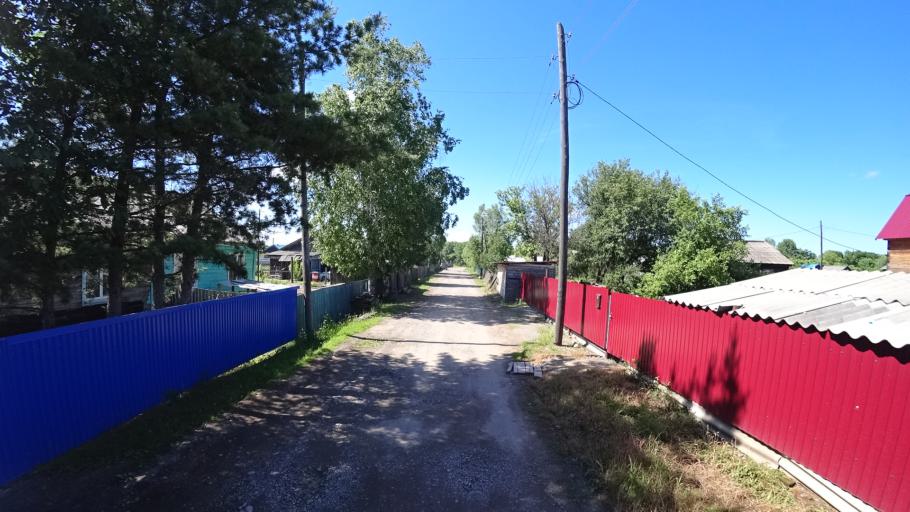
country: RU
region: Khabarovsk Krai
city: Khor
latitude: 47.8879
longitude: 135.0254
